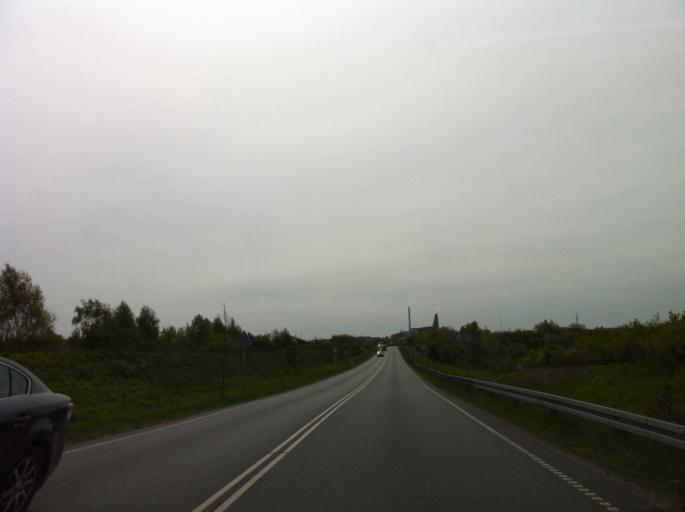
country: DK
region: Zealand
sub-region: Roskilde Kommune
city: Roskilde
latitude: 55.6647
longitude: 12.1161
